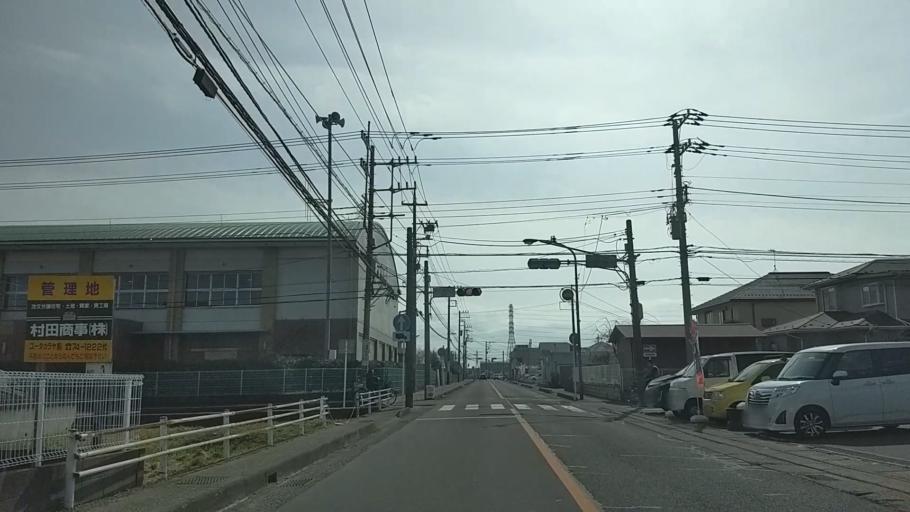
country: JP
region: Kanagawa
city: Chigasaki
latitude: 35.3623
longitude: 139.3853
